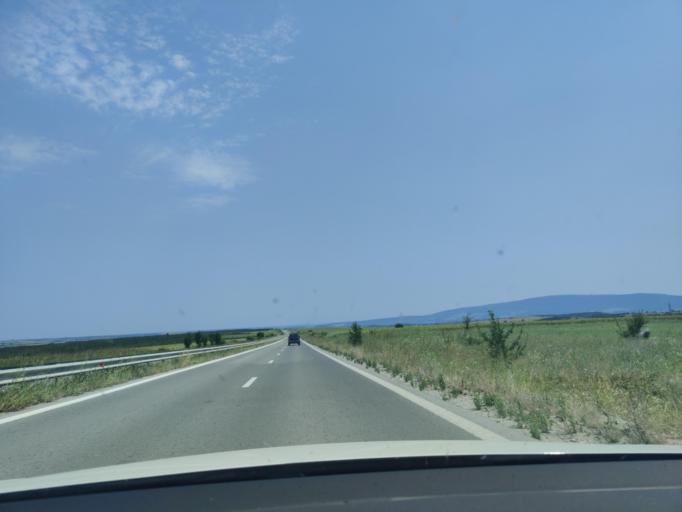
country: BG
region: Montana
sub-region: Obshtina Montana
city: Montana
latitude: 43.4268
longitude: 23.1718
